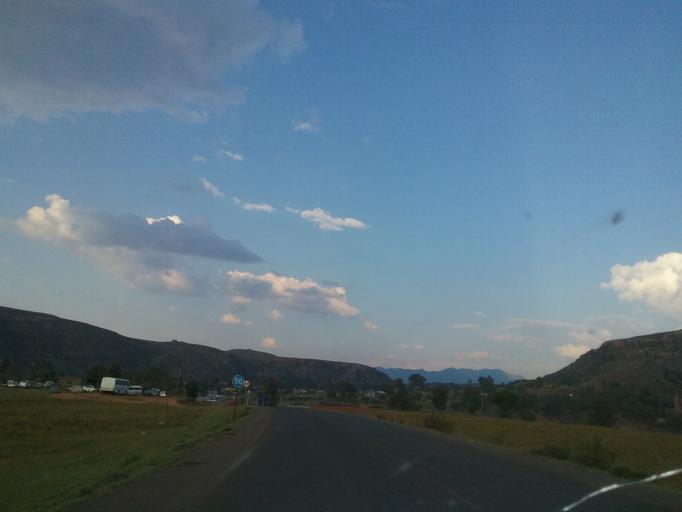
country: LS
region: Quthing
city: Quthing
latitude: -30.3983
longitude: 27.6571
